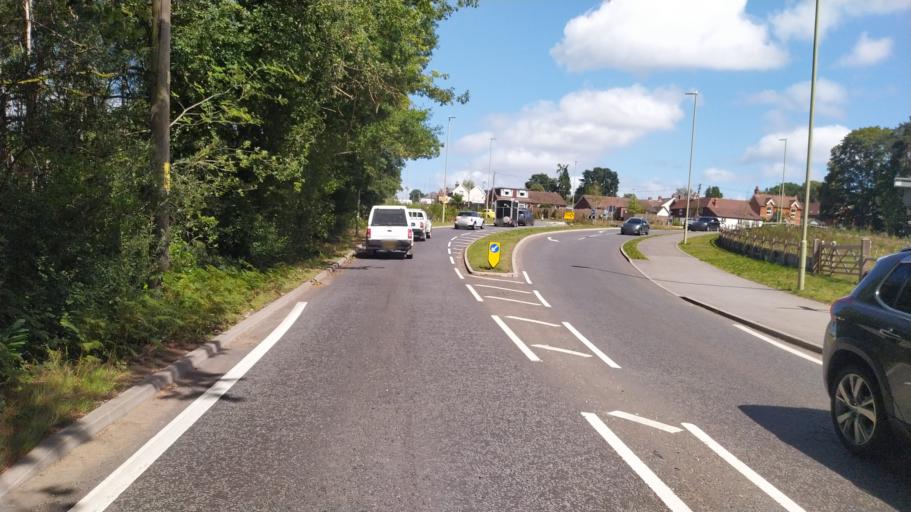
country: GB
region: England
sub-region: Hampshire
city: Bordon
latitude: 51.0989
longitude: -0.8708
